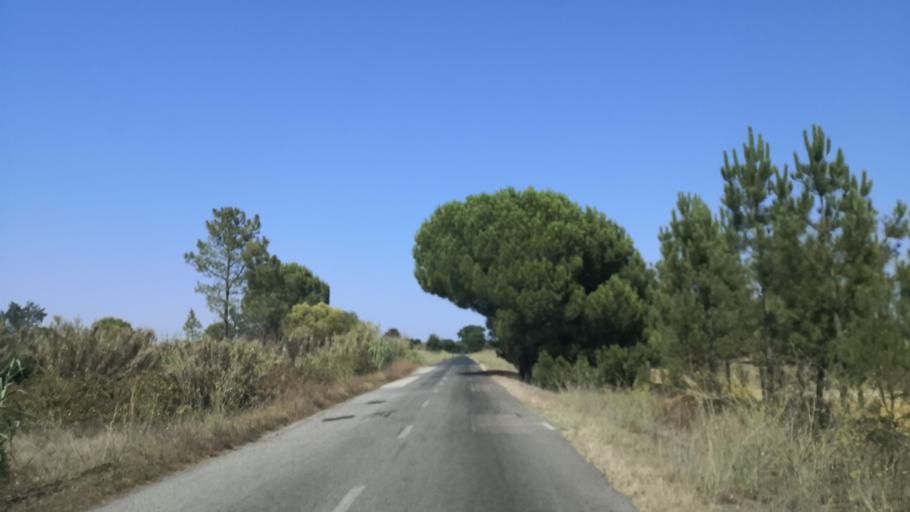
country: PT
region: Santarem
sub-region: Benavente
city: Poceirao
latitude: 38.7282
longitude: -8.7036
